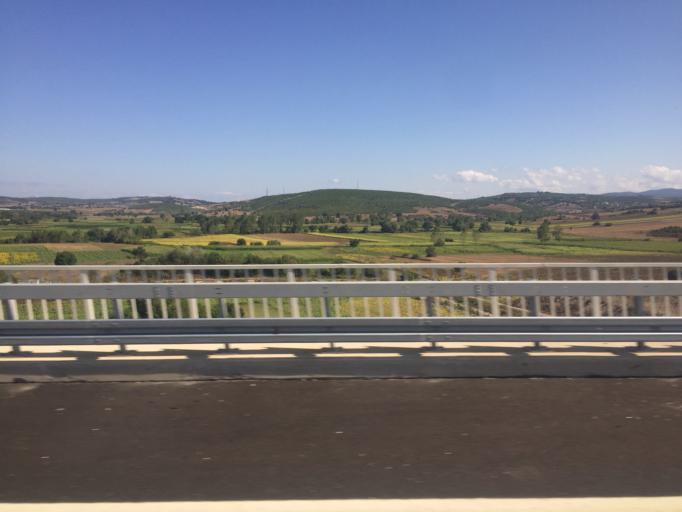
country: TR
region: Bursa
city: Mahmudiye
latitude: 40.2640
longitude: 28.6657
